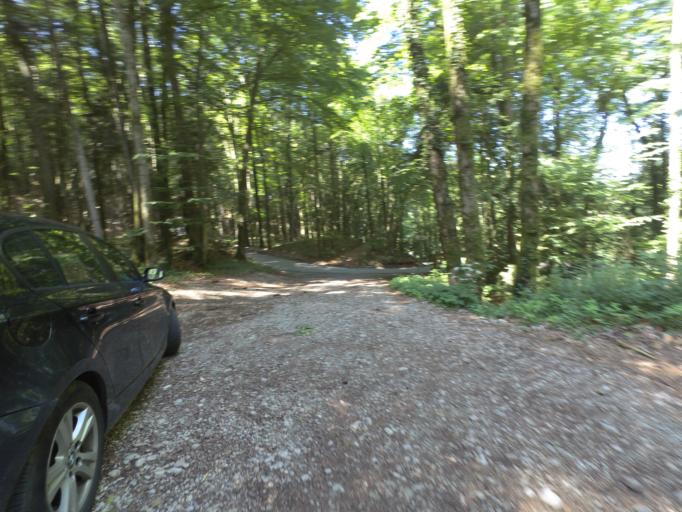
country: AT
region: Salzburg
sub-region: Politischer Bezirk Salzburg-Umgebung
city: Elsbethen
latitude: 47.7672
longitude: 13.0957
